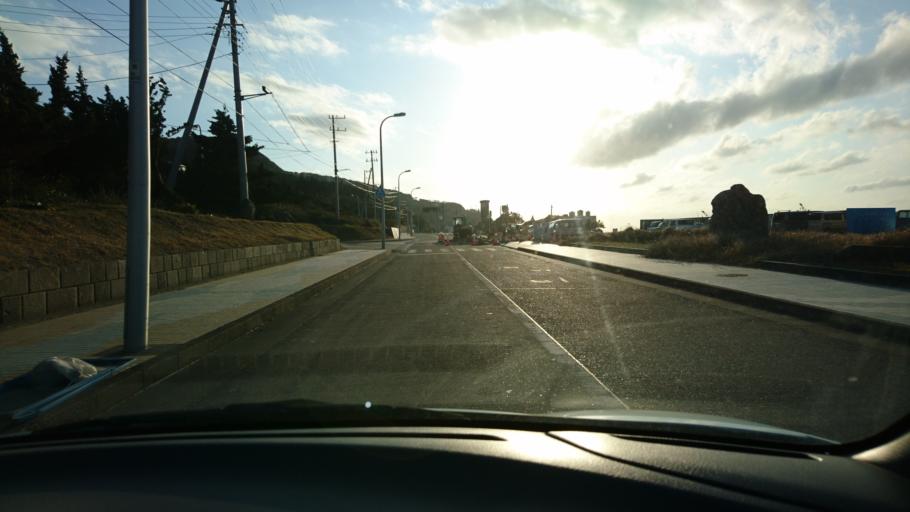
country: JP
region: Shizuoka
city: Shimoda
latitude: 34.3713
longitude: 139.2500
